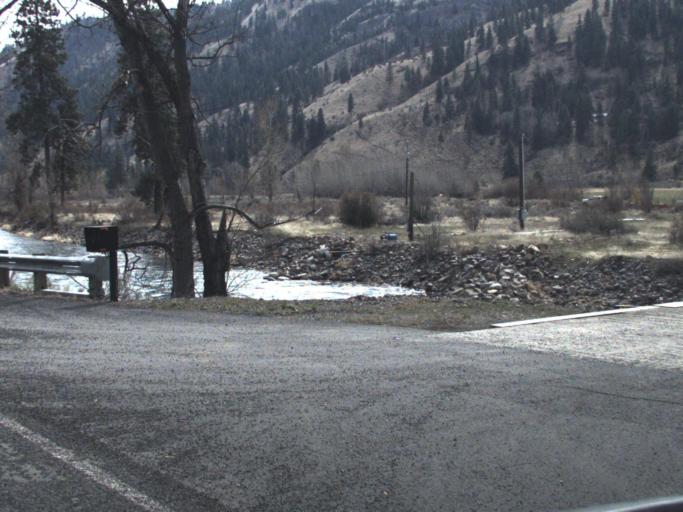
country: US
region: Washington
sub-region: Yakima County
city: Tieton
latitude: 46.7884
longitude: -120.8690
